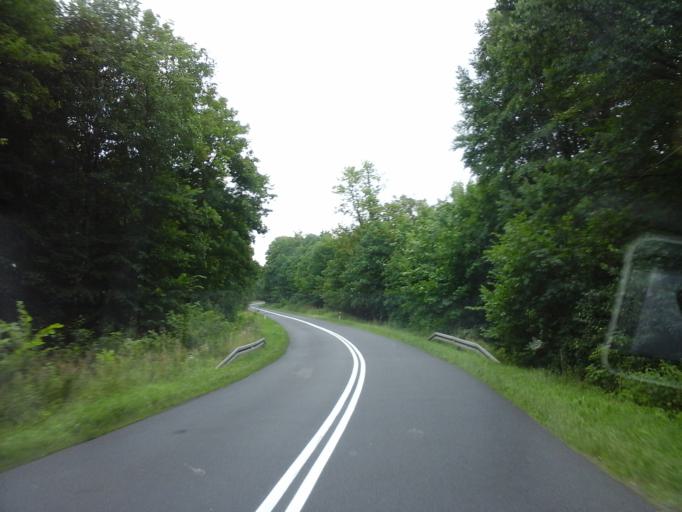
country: PL
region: West Pomeranian Voivodeship
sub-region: Powiat choszczenski
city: Pelczyce
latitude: 52.9369
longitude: 15.3727
